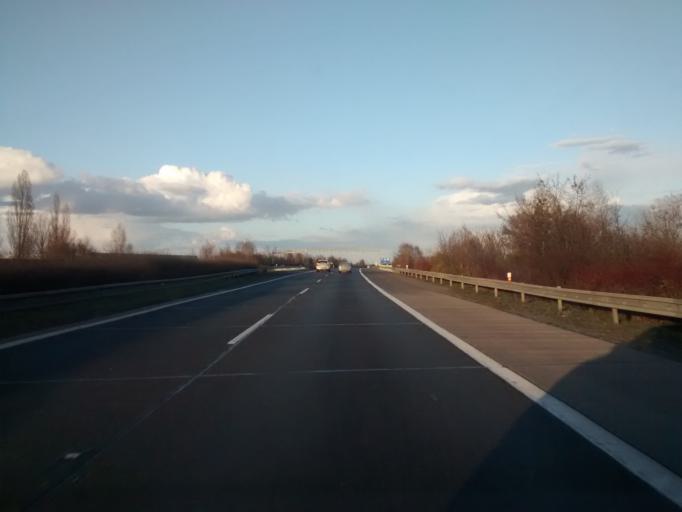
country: CZ
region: Praha
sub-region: Praha 20
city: Horni Pocernice
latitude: 50.1052
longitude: 14.6231
